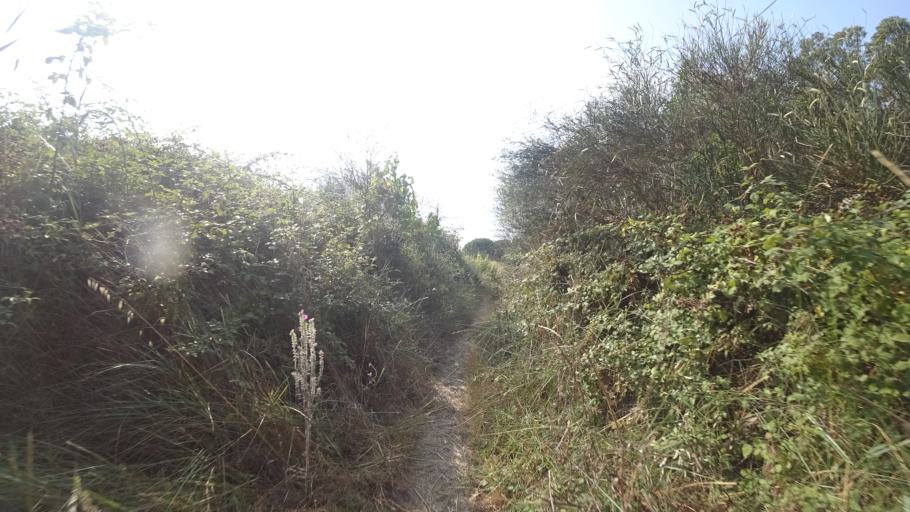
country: FR
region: Languedoc-Roussillon
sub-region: Departement des Pyrenees-Orientales
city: Canet-en-Roussillon
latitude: 42.6897
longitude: 3.0268
